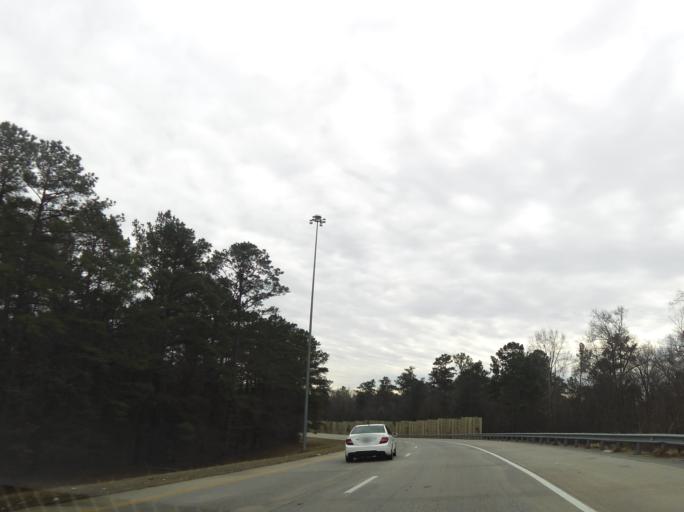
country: US
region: Georgia
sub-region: Bibb County
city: West Point
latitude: 32.8796
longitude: -83.7704
